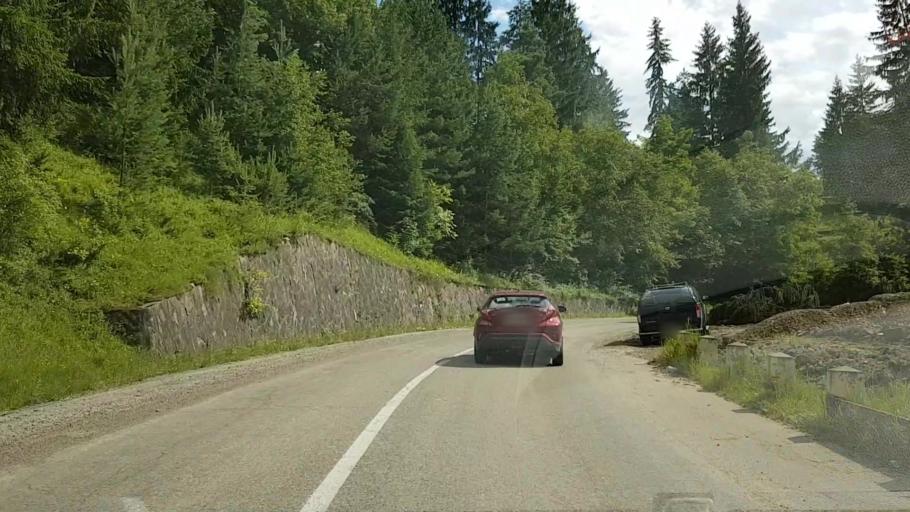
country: RO
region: Neamt
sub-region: Comuna Hangu
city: Hangu
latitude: 47.0141
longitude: 26.0829
